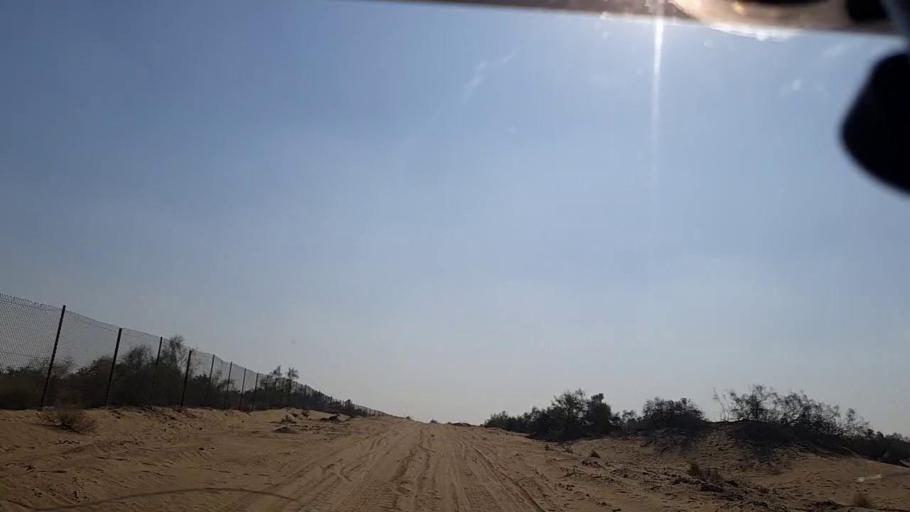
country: PK
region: Sindh
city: Khanpur
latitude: 27.5624
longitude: 69.3887
